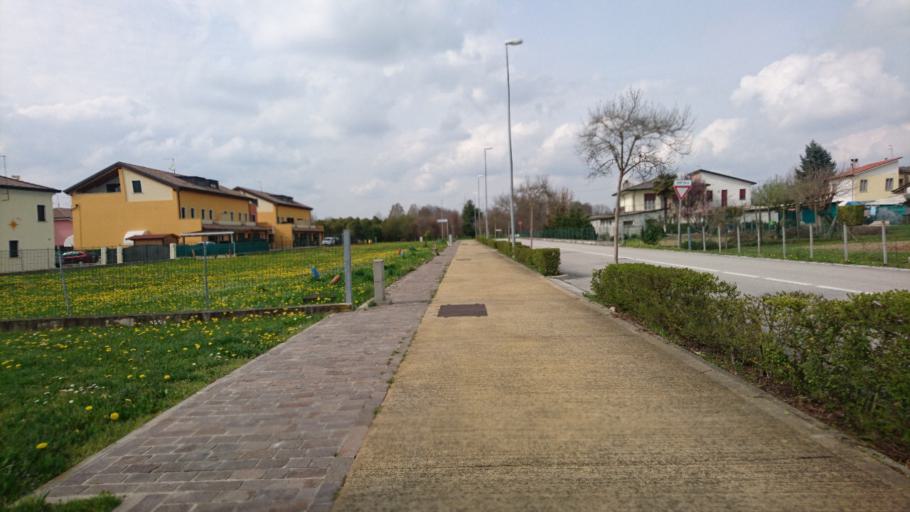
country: IT
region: Veneto
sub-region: Provincia di Padova
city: Curtarolo
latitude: 45.5093
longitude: 11.8238
